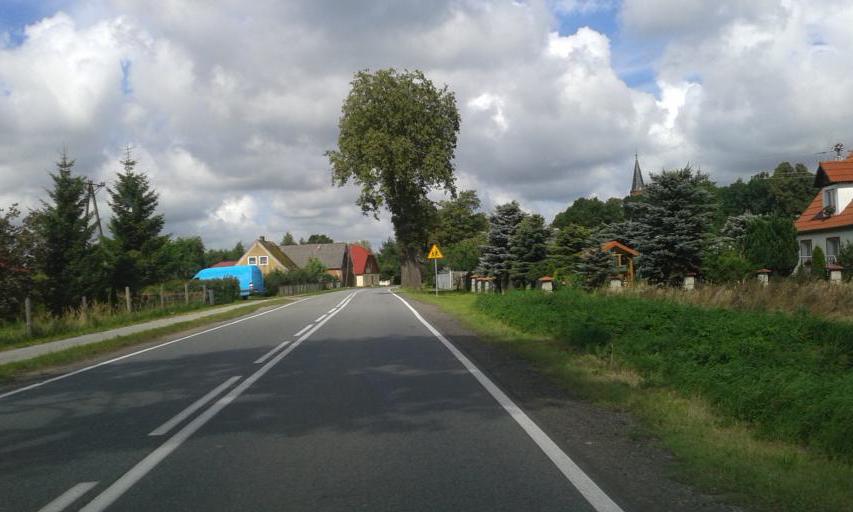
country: PL
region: West Pomeranian Voivodeship
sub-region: Powiat slawienski
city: Darlowo
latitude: 54.3567
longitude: 16.5178
